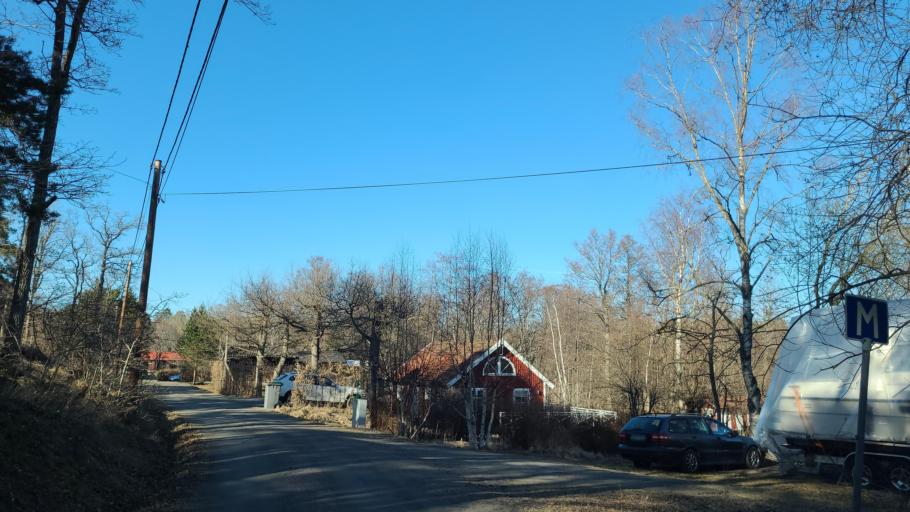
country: SE
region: Stockholm
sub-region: Varmdo Kommun
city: Holo
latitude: 59.3570
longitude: 18.6653
